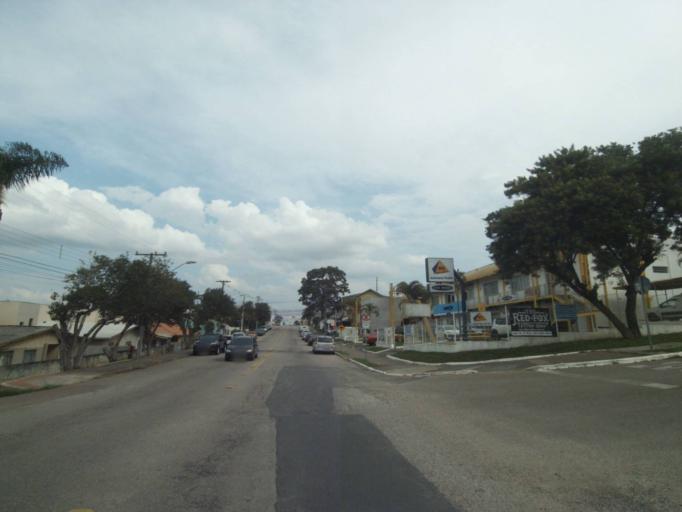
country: BR
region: Parana
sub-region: Pinhais
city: Pinhais
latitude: -25.4046
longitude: -49.2101
